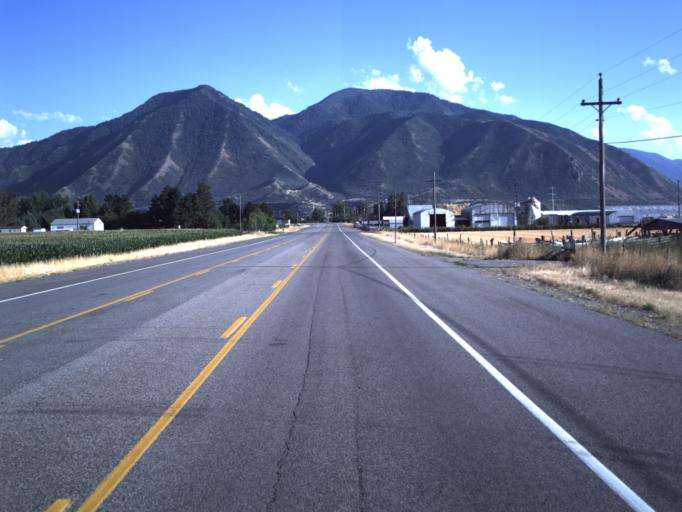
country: US
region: Utah
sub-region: Utah County
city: Mapleton
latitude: 40.1103
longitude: -111.5978
